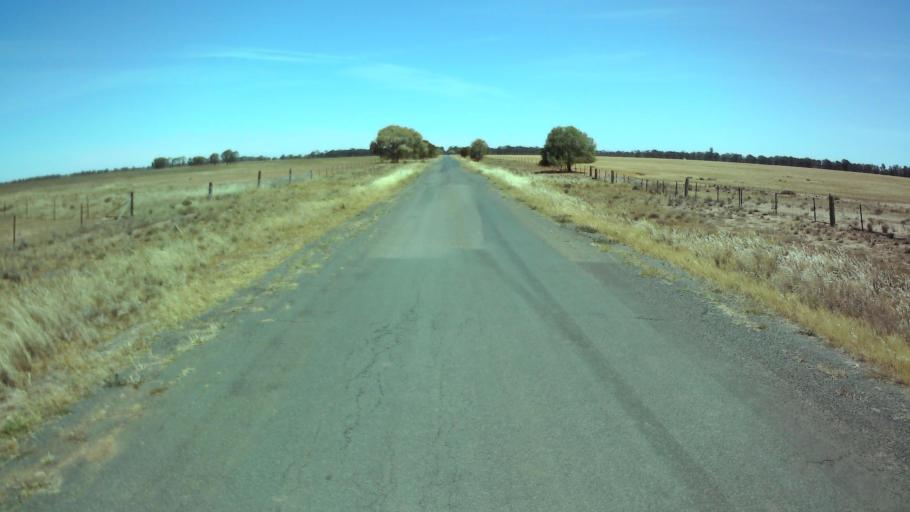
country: AU
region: New South Wales
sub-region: Weddin
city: Grenfell
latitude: -33.8522
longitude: 147.6954
